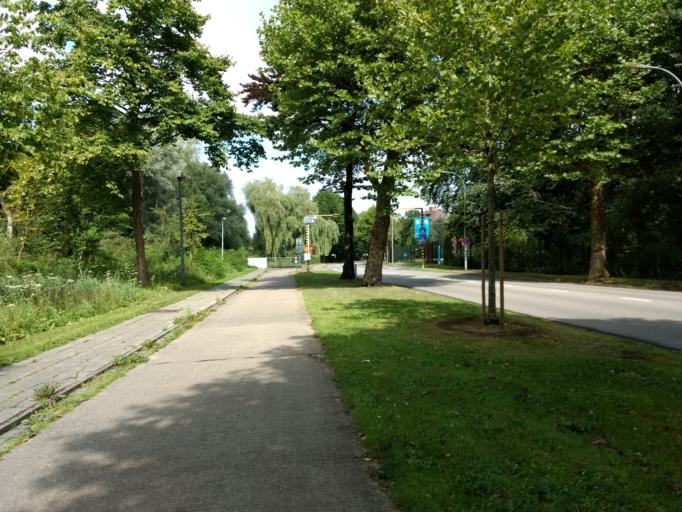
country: BE
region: Flanders
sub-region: Provincie Vlaams-Brabant
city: Leuven
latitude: 50.8948
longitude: 4.7170
